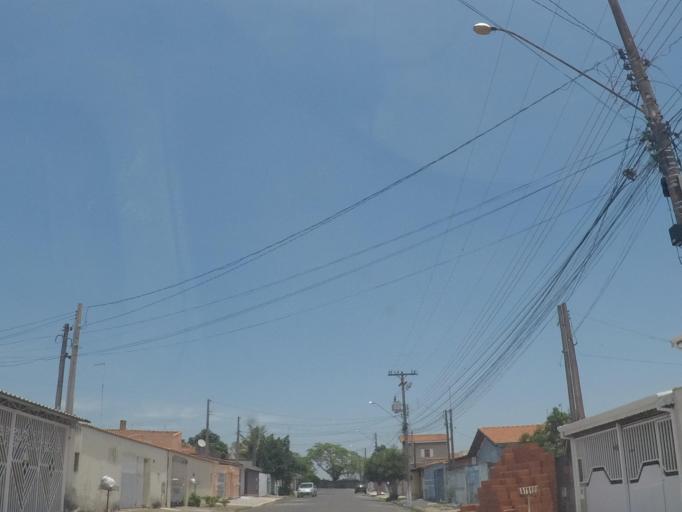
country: BR
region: Sao Paulo
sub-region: Hortolandia
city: Hortolandia
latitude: -22.8578
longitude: -47.1859
